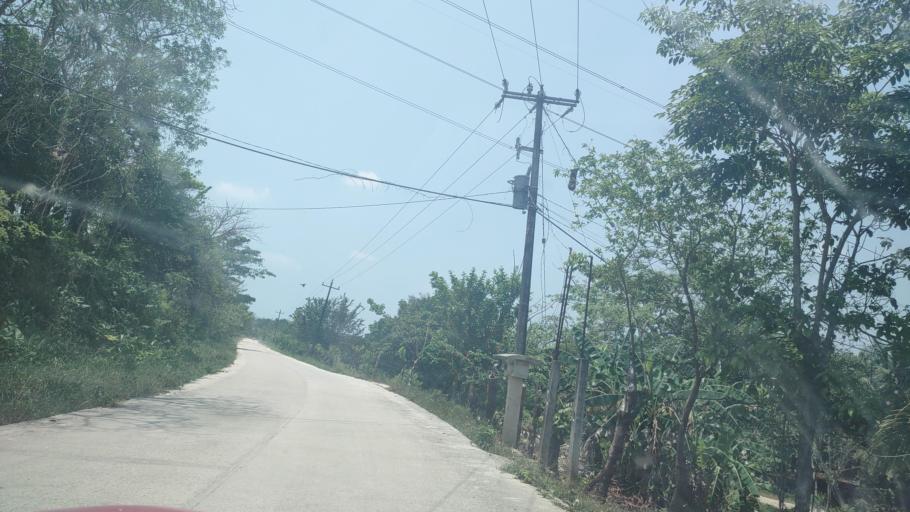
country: MX
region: Tabasco
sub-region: Huimanguillo
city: Francisco Rueda
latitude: 17.6915
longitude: -94.0477
